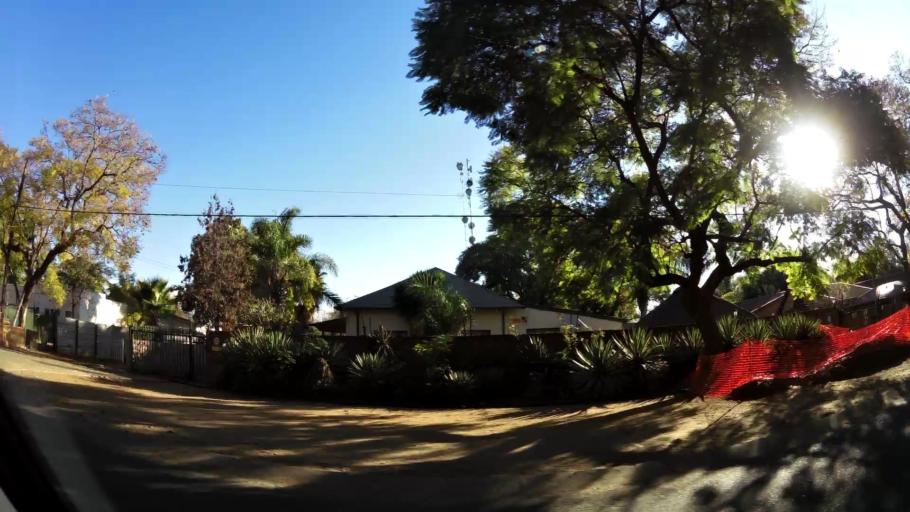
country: ZA
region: Limpopo
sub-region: Capricorn District Municipality
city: Polokwane
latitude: -23.9025
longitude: 29.4565
